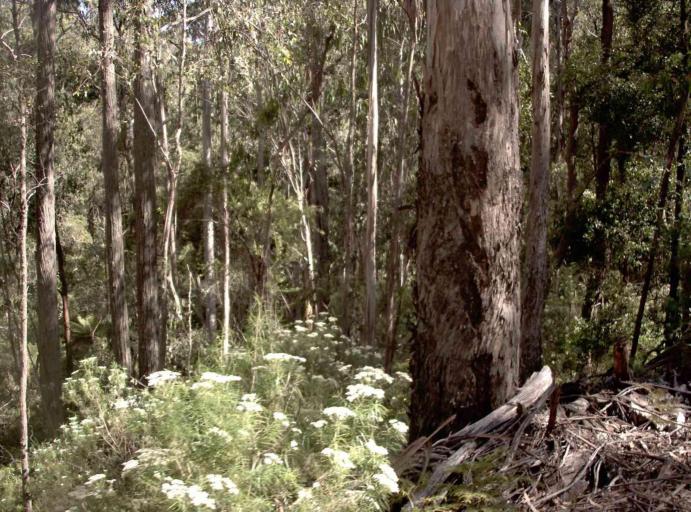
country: AU
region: New South Wales
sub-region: Bombala
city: Bombala
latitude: -37.2872
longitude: 148.7150
